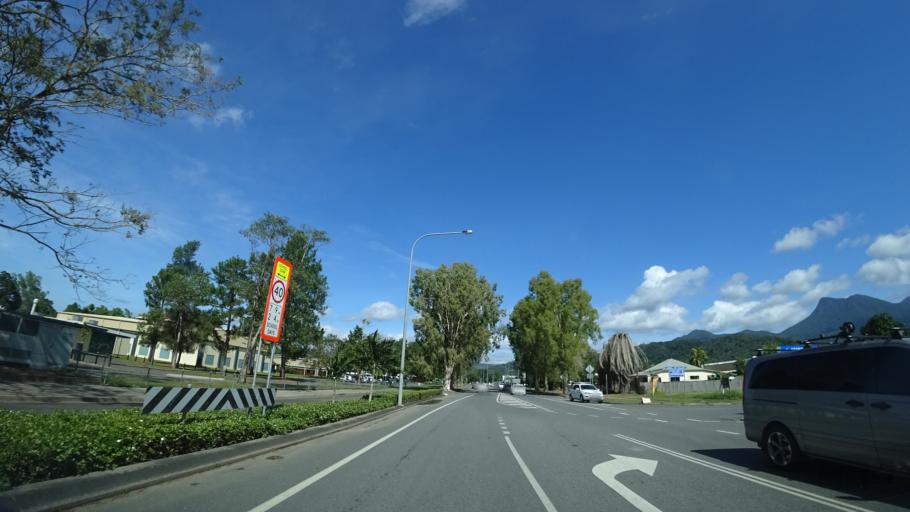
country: AU
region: Queensland
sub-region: Cairns
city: Port Douglas
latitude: -16.4638
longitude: 145.3734
